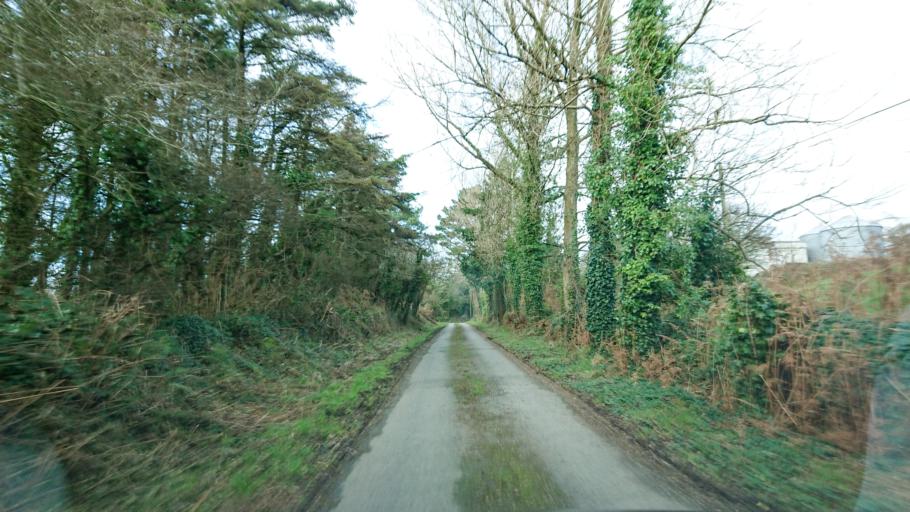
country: IE
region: Munster
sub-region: Waterford
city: Tra Mhor
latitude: 52.1636
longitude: -7.2734
